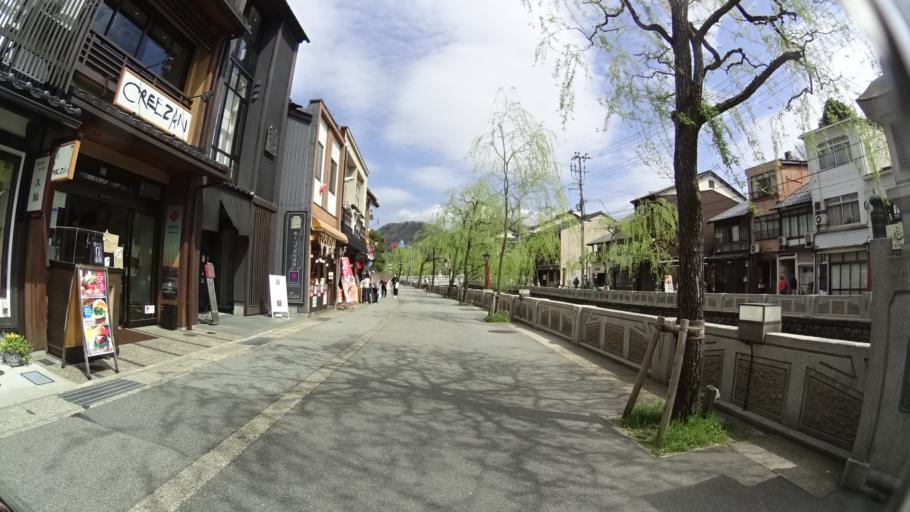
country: JP
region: Hyogo
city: Toyooka
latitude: 35.6213
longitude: 134.8082
